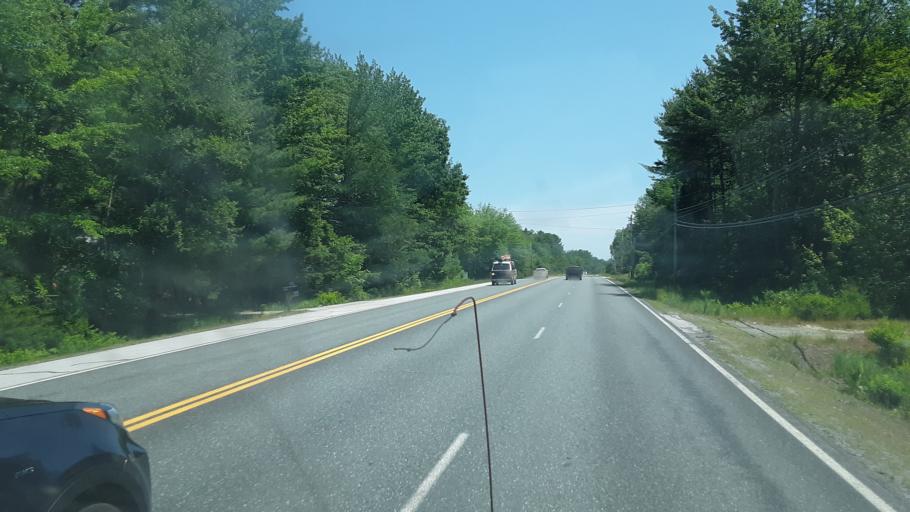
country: US
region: Maine
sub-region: Hancock County
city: Hancock
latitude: 44.5380
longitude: -68.2965
